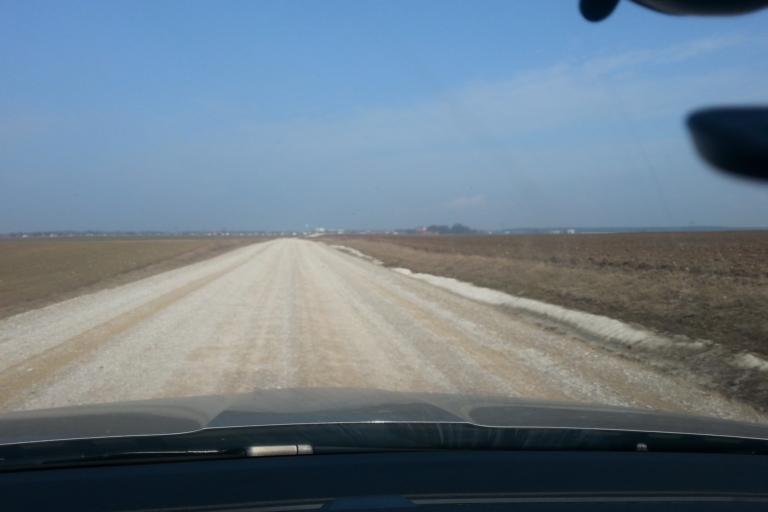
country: LT
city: Trakai
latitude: 54.5917
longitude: 24.9772
